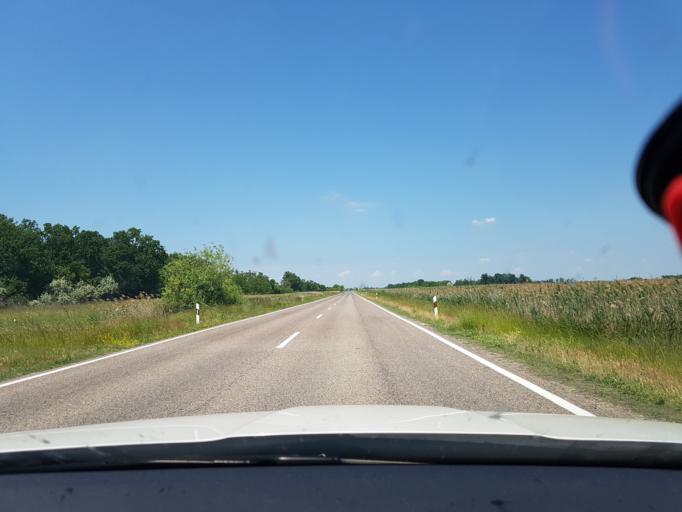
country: HU
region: Hajdu-Bihar
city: Egyek
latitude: 47.5621
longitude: 20.8633
